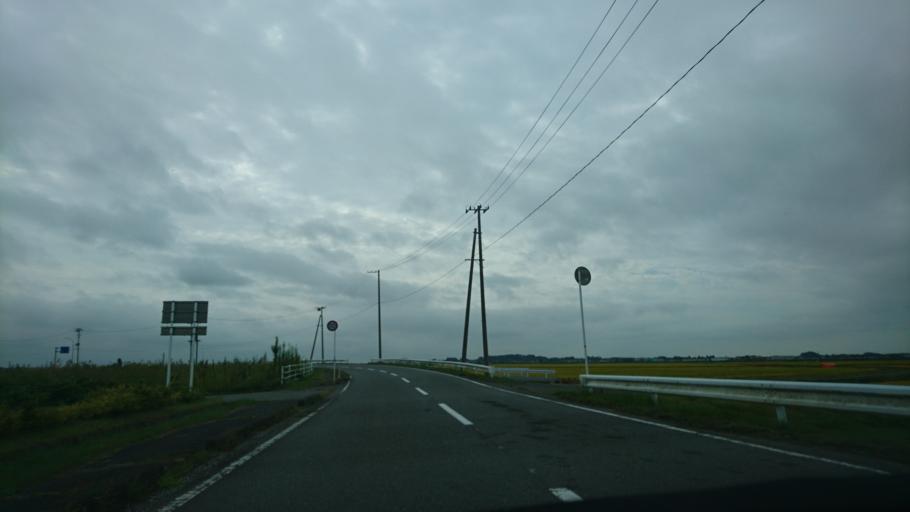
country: JP
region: Iwate
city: Ichinoseki
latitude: 38.8040
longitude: 141.1125
